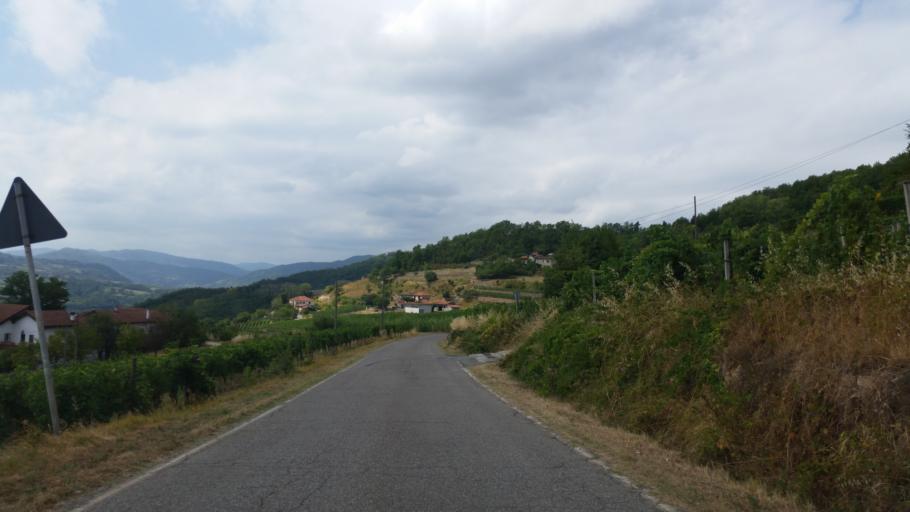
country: IT
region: Piedmont
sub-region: Provincia di Asti
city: Vesime
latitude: 44.6452
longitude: 8.2272
